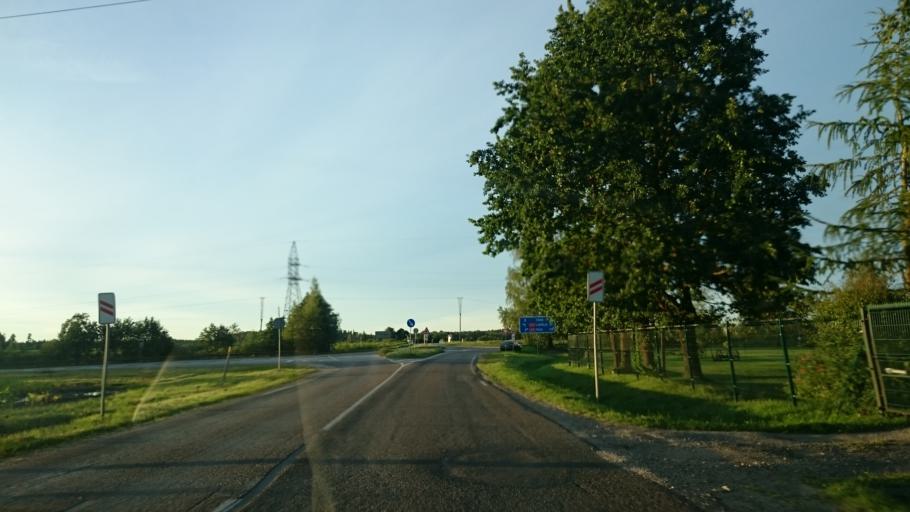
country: LV
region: Saldus Rajons
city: Saldus
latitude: 56.6880
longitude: 22.5052
